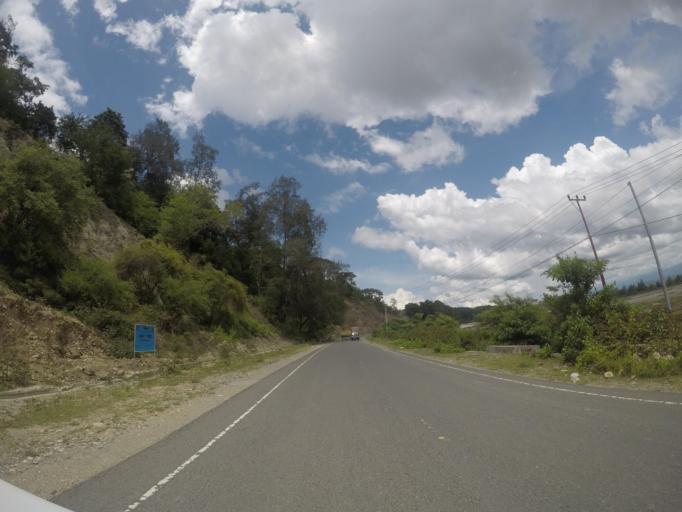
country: TL
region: Bobonaro
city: Maliana
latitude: -8.9589
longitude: 125.1088
